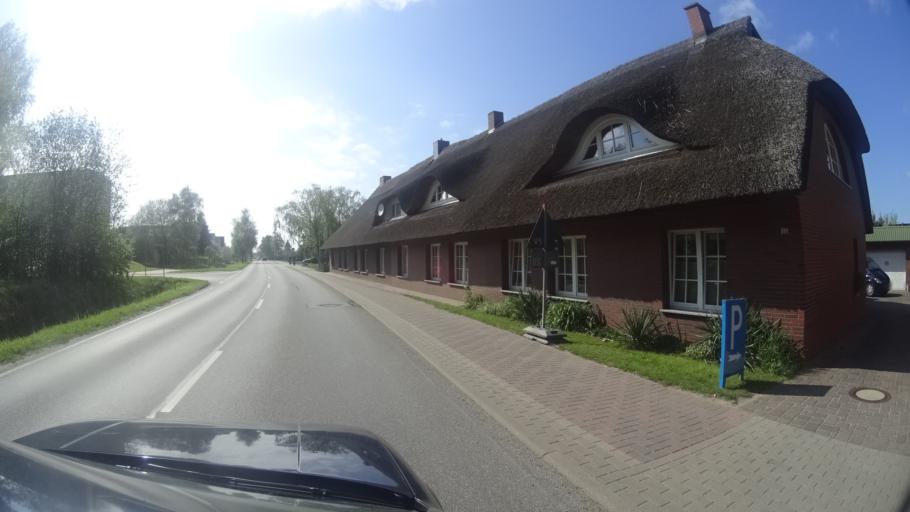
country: DE
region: Mecklenburg-Vorpommern
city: Rovershagen
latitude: 54.1765
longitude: 12.2339
